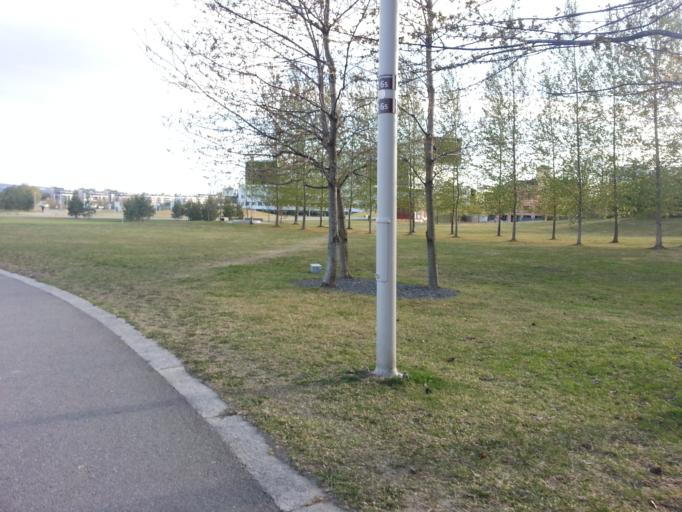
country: NO
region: Akershus
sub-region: Baerum
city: Lysaker
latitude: 59.8988
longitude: 10.6331
